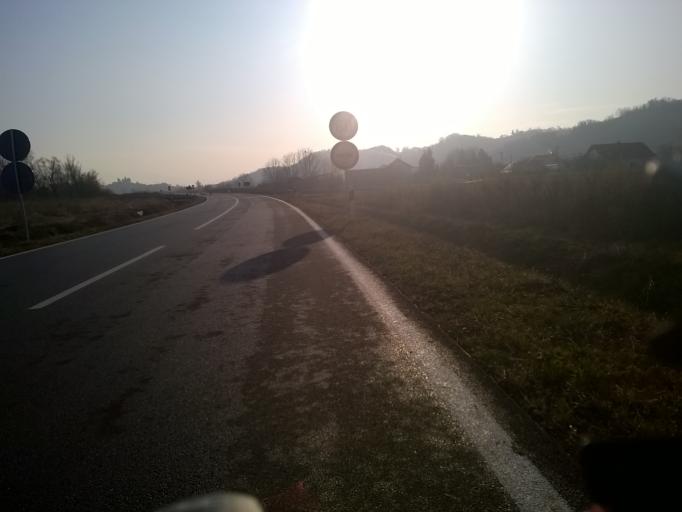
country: HR
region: Krapinsko-Zagorska
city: Zabok
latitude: 46.0575
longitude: 15.9129
